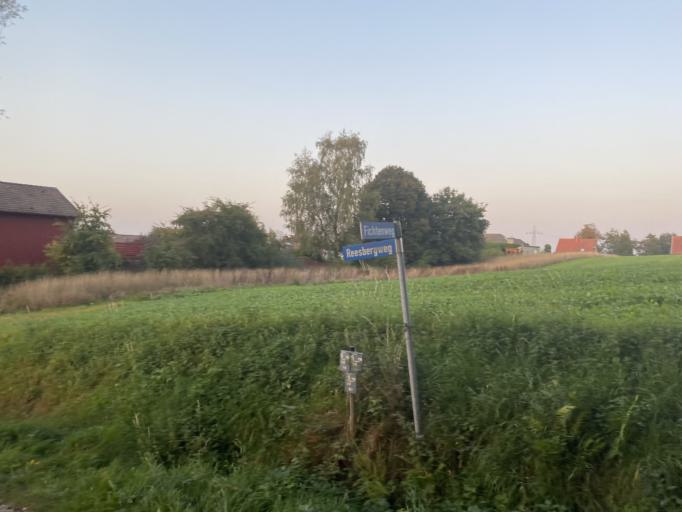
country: DE
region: North Rhine-Westphalia
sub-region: Regierungsbezirk Detmold
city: Kirchlengern
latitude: 52.1827
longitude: 8.6365
